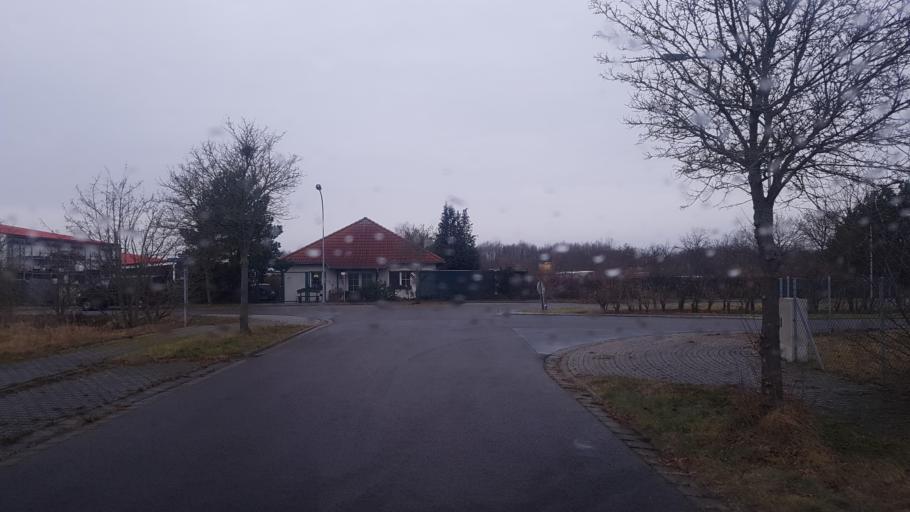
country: DE
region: Brandenburg
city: Schwarzheide
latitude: 51.4719
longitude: 13.8292
